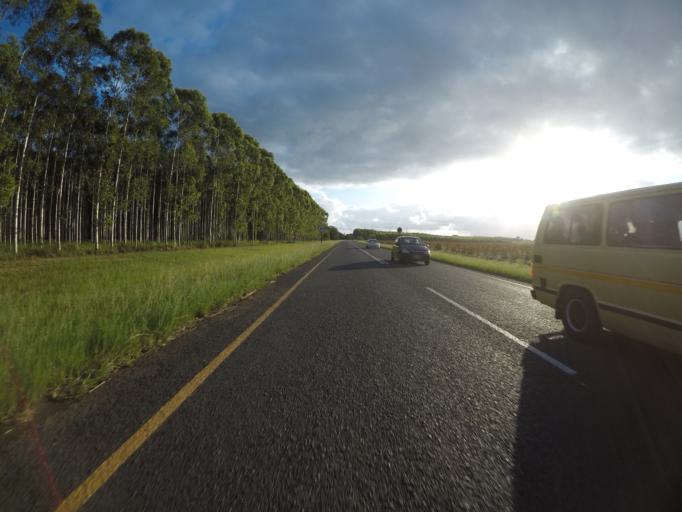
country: ZA
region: KwaZulu-Natal
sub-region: uMkhanyakude District Municipality
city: Mtubatuba
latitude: -28.4101
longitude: 32.1963
